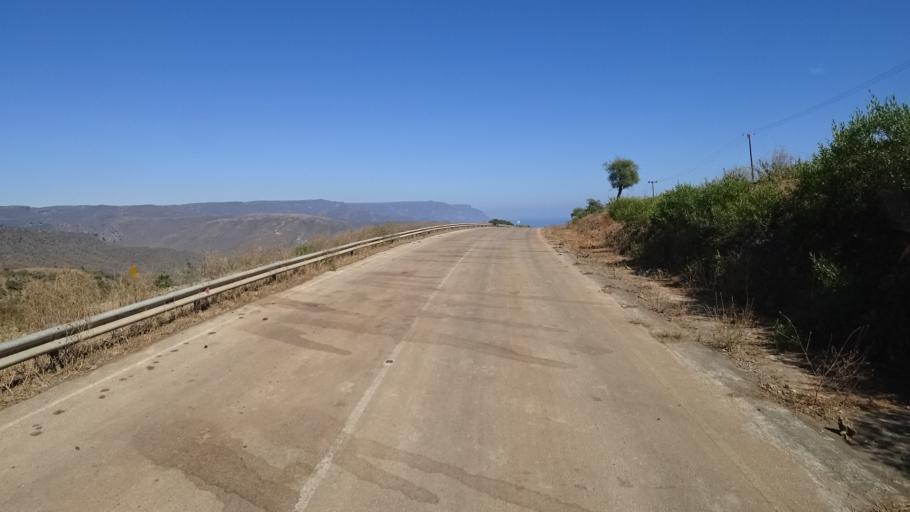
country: YE
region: Al Mahrah
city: Hawf
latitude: 16.7441
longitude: 53.3734
